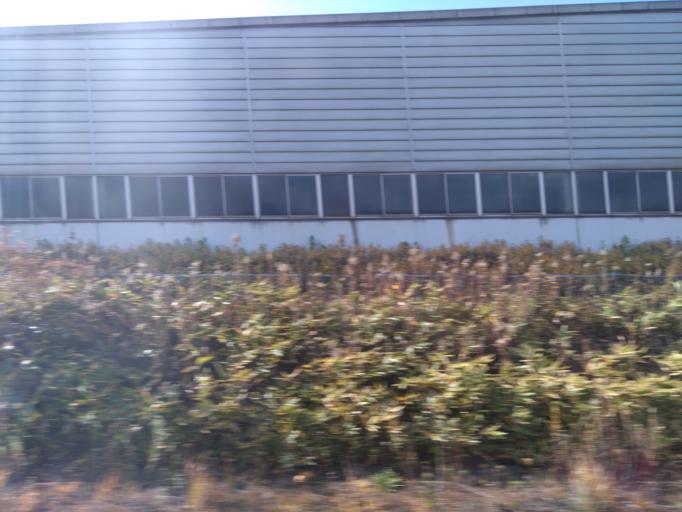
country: JP
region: Hokkaido
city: Kitahiroshima
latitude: 42.9268
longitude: 141.5729
